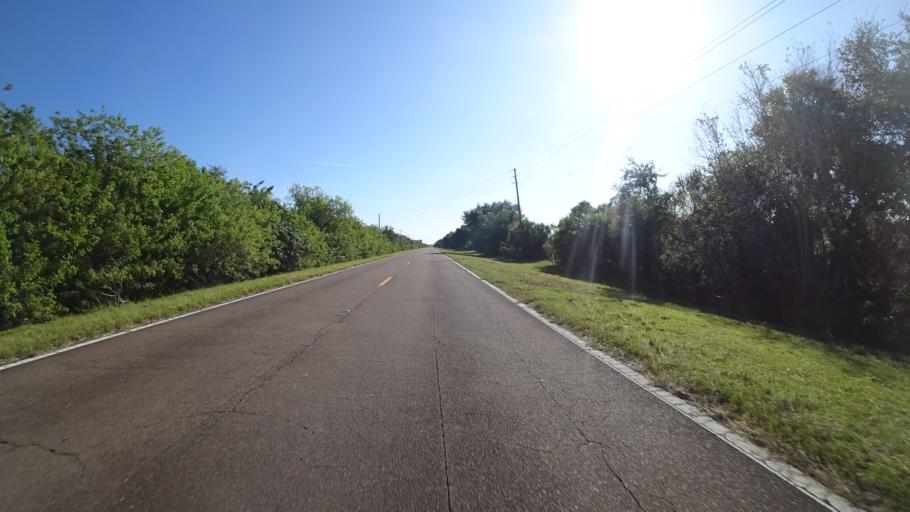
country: US
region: Florida
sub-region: Hillsborough County
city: Ruskin
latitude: 27.6538
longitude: -82.4825
